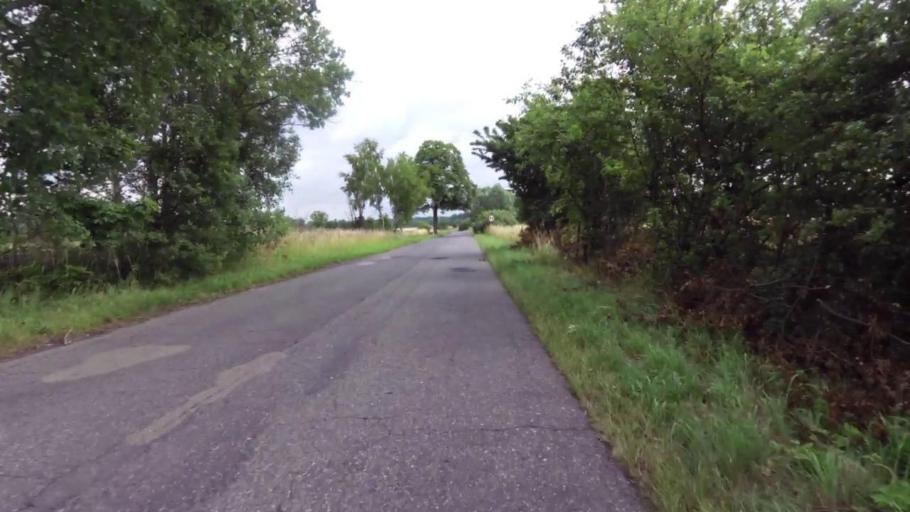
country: PL
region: West Pomeranian Voivodeship
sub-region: Powiat mysliborski
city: Mysliborz
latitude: 52.9642
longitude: 14.8911
